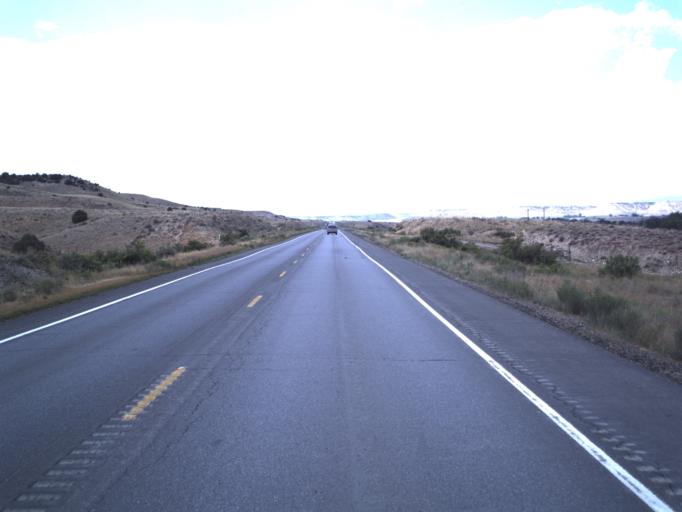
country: US
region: Utah
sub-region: Duchesne County
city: Duchesne
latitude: 40.1602
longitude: -110.2690
